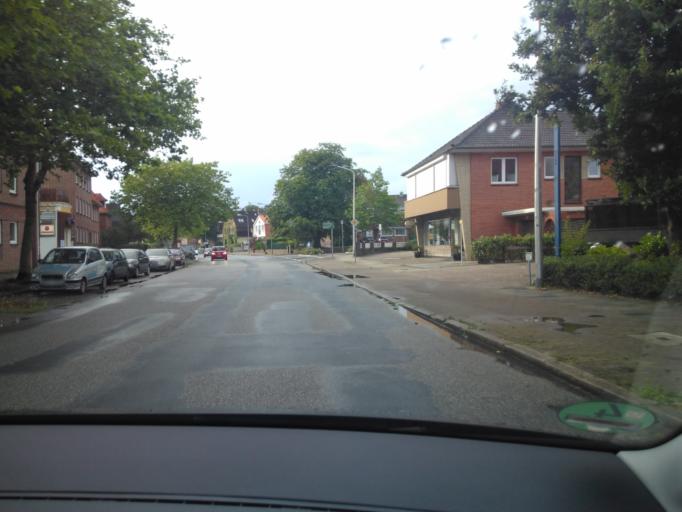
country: DE
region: Lower Saxony
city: Cuxhaven
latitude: 53.8696
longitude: 8.6922
